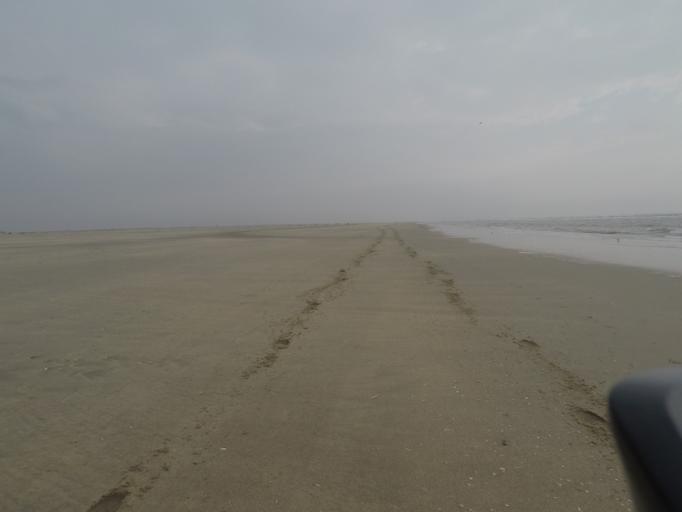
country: DE
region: Schleswig-Holstein
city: List
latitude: 55.1547
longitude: 8.4763
